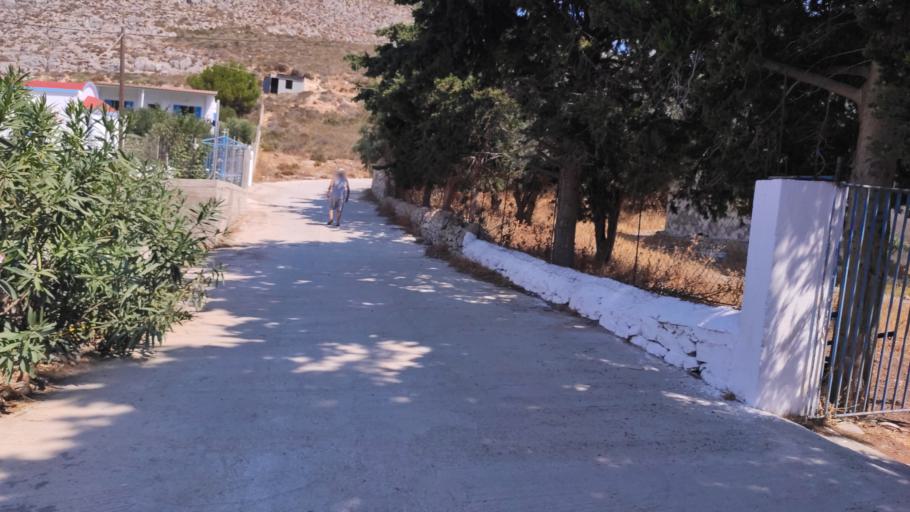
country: GR
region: South Aegean
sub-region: Nomos Dodekanisou
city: Pylion
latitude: 36.9339
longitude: 27.1323
